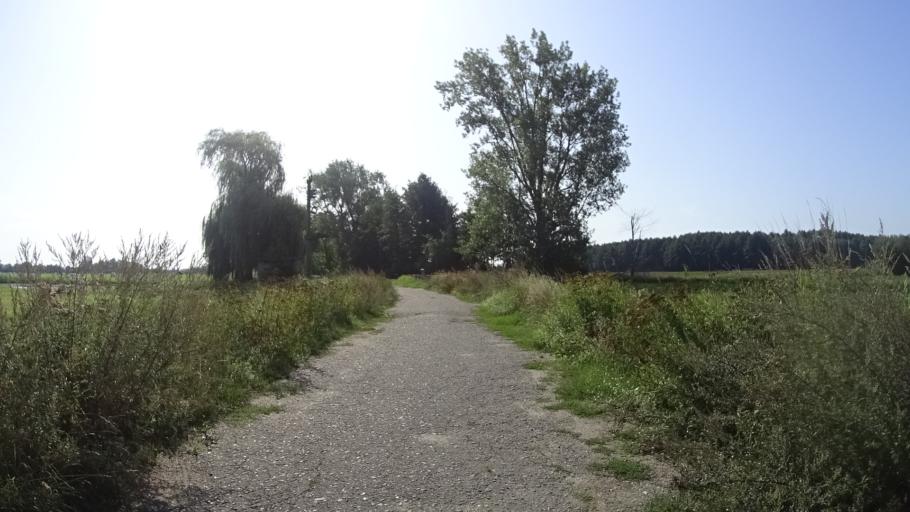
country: DE
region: Brandenburg
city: Neu Zauche
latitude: 51.9175
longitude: 14.0359
